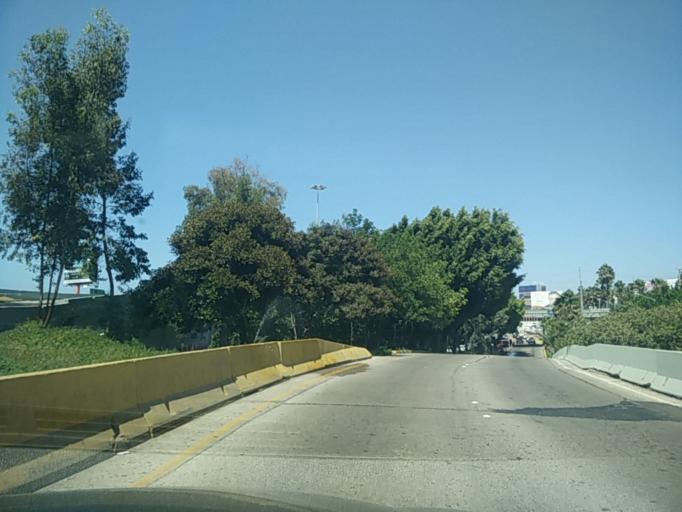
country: MX
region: Baja California
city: Tijuana
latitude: 32.5392
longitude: -117.0259
